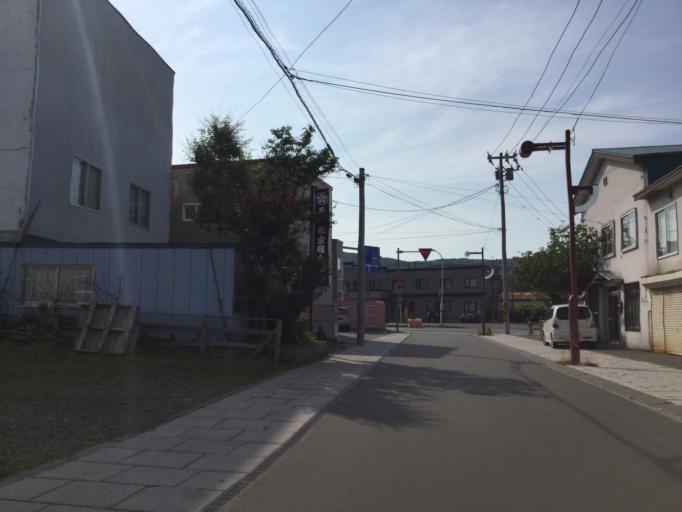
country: JP
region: Hokkaido
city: Wakkanai
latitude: 45.3992
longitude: 141.6815
